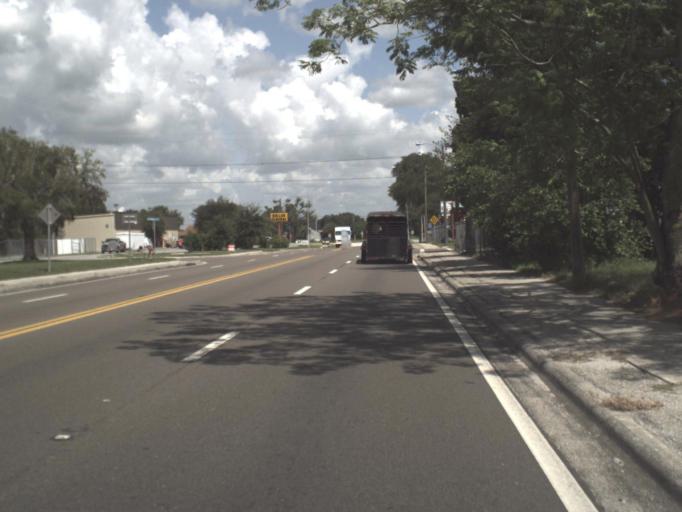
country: US
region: Florida
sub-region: Hardee County
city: Zolfo Springs
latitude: 27.4948
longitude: -81.7963
